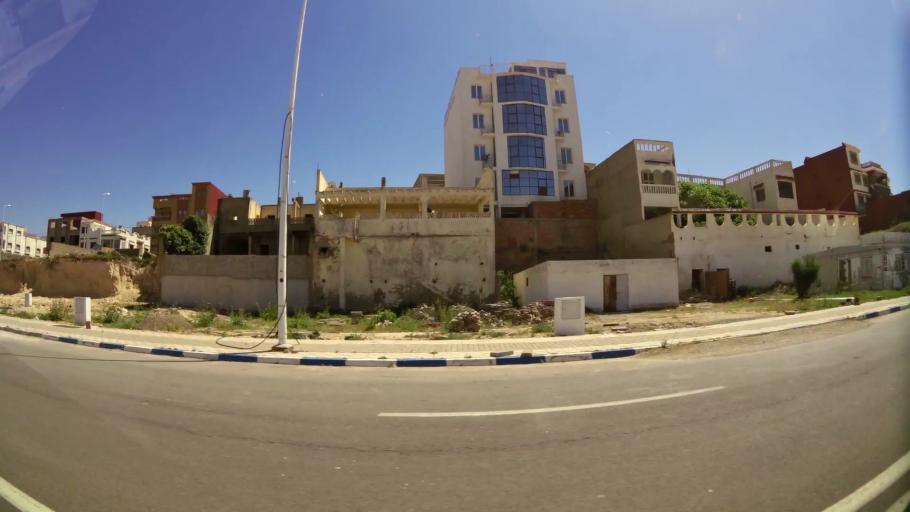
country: MA
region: Oriental
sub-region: Berkane-Taourirt
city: Madagh
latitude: 35.1383
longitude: -2.4208
